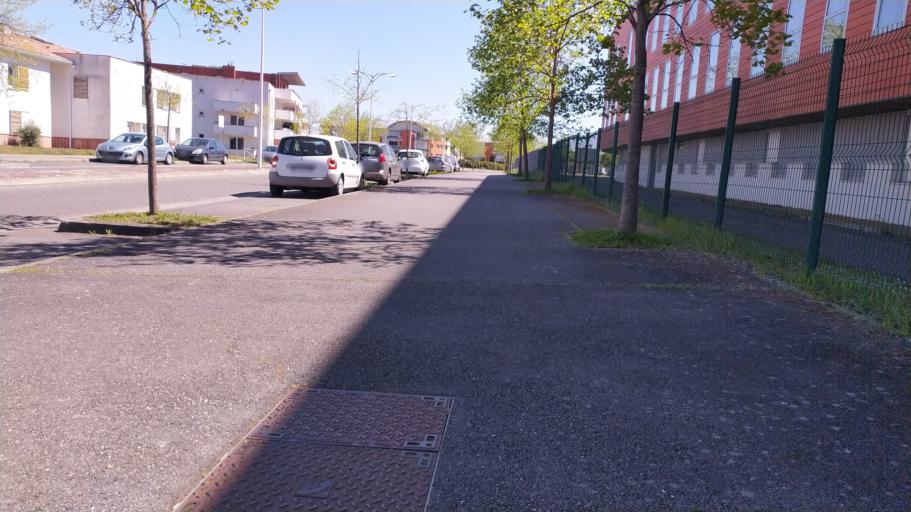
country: FR
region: Midi-Pyrenees
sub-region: Departement de la Haute-Garonne
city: Tournefeuille
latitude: 43.5778
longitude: 1.3121
